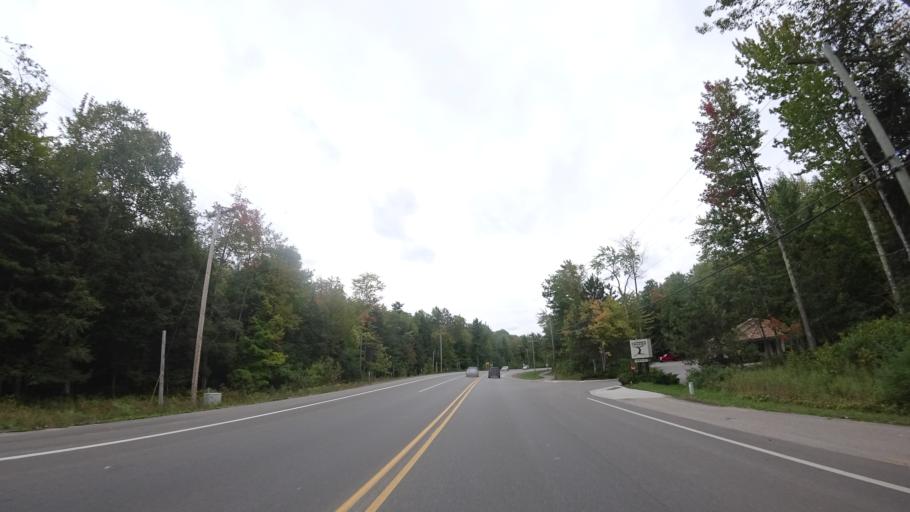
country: US
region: Michigan
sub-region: Emmet County
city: Petoskey
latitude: 45.4111
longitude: -84.9030
